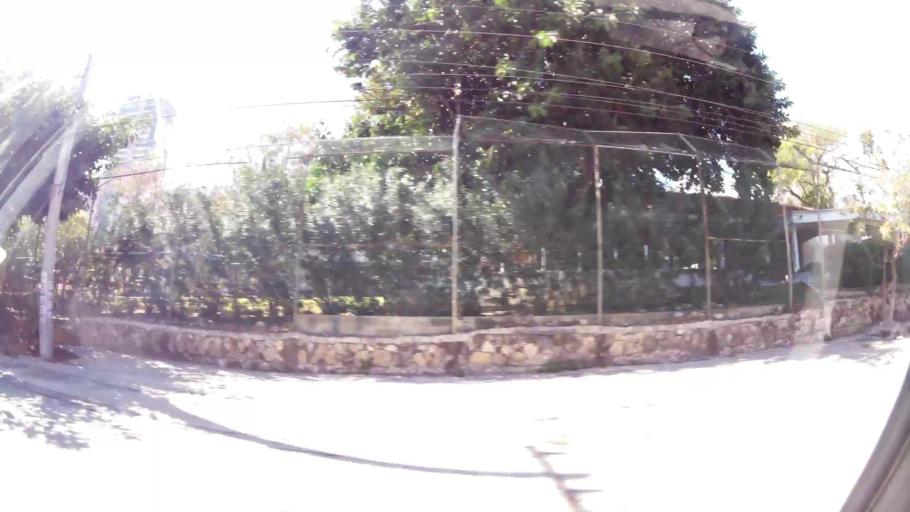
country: CO
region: Atlantico
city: Barranquilla
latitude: 11.0124
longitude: -74.8118
